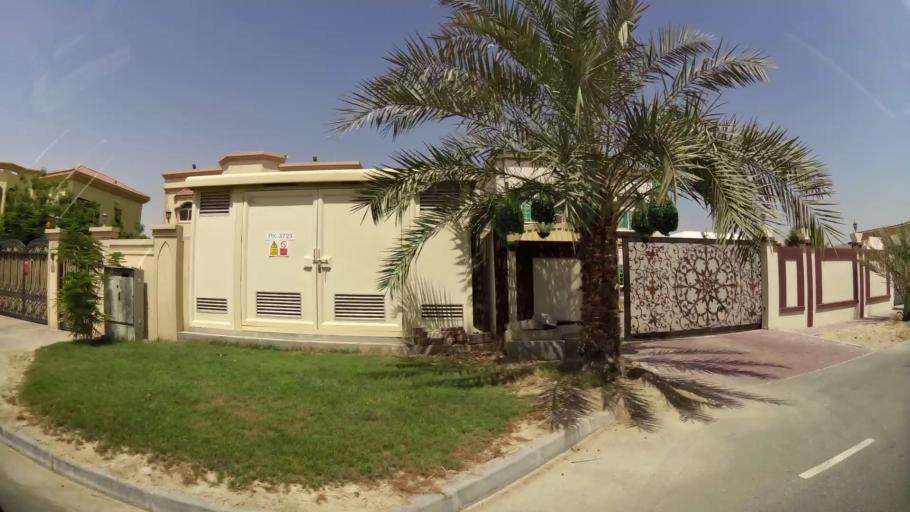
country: AE
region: Ash Shariqah
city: Sharjah
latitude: 25.1822
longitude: 55.4189
